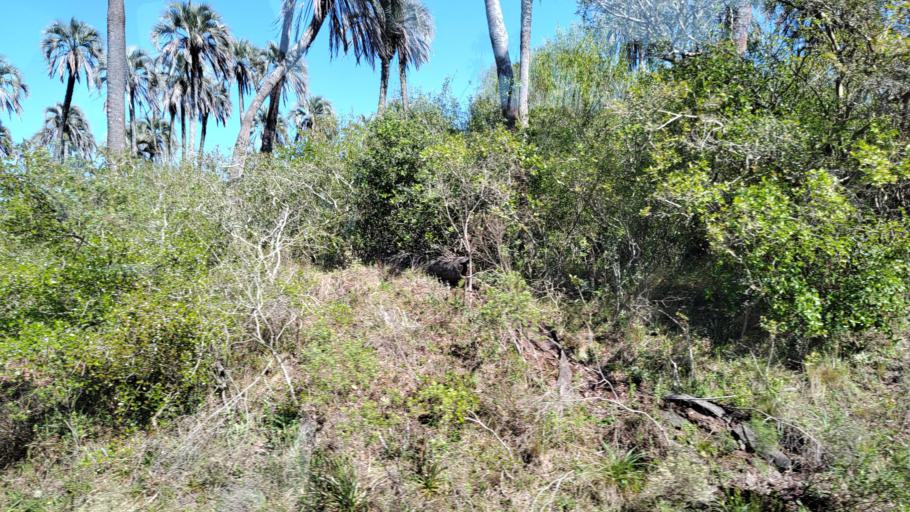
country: AR
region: Entre Rios
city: Ubajay
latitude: -31.8879
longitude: -58.2409
